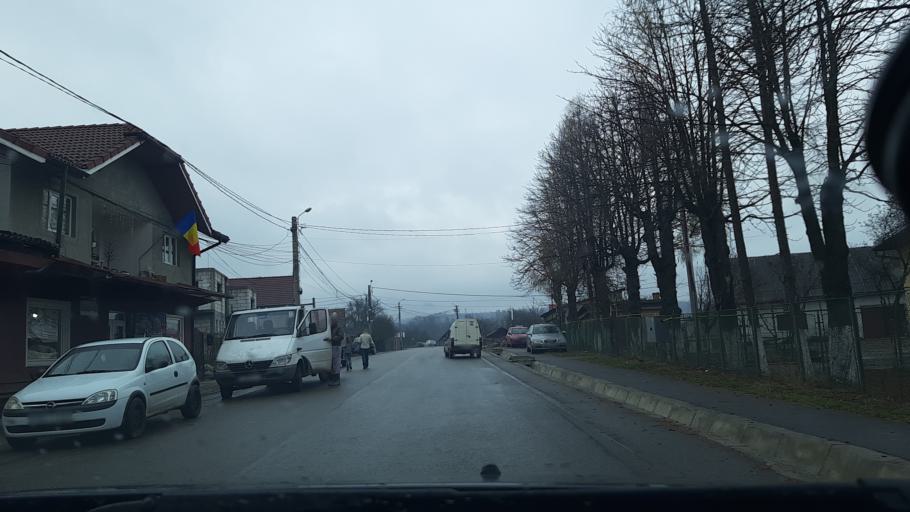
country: RO
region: Hunedoara
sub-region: Oras Petrila
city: Petrila
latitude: 45.4418
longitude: 23.4116
